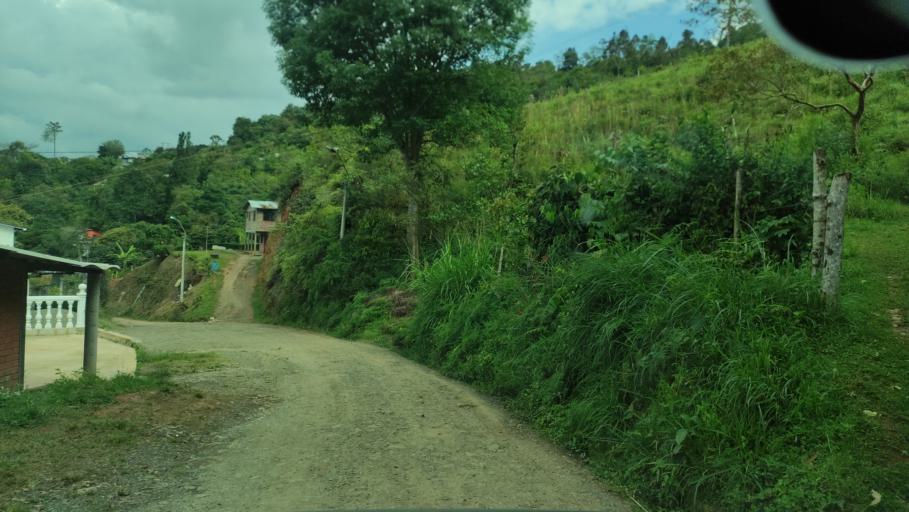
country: CO
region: Valle del Cauca
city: Cali
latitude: 3.4532
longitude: -76.6346
